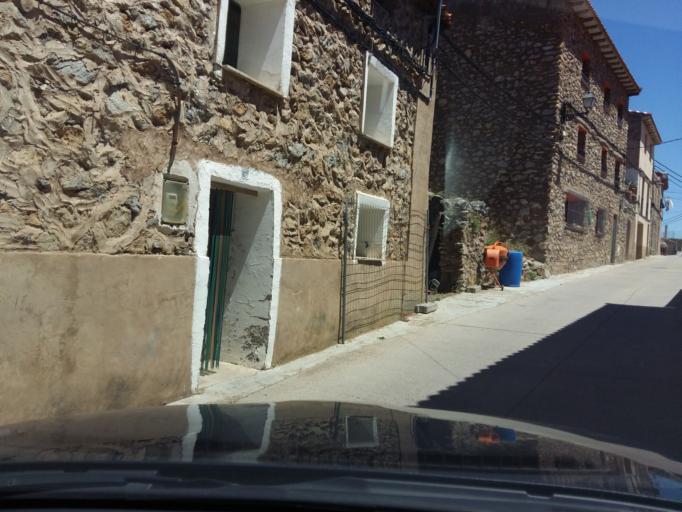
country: ES
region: Aragon
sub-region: Provincia de Zaragoza
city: Alcala de Moncayo
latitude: 41.7790
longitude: -1.7181
